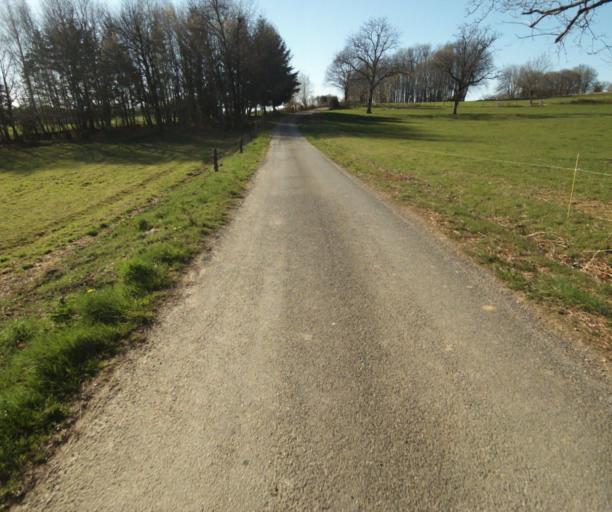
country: FR
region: Limousin
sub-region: Departement de la Correze
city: Seilhac
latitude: 45.3908
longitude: 1.6989
